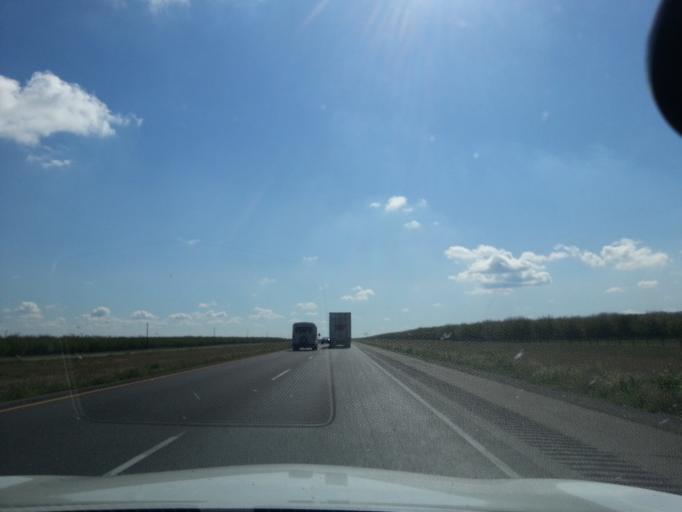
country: US
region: California
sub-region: Fresno County
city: San Joaquin
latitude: 36.4124
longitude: -120.3736
